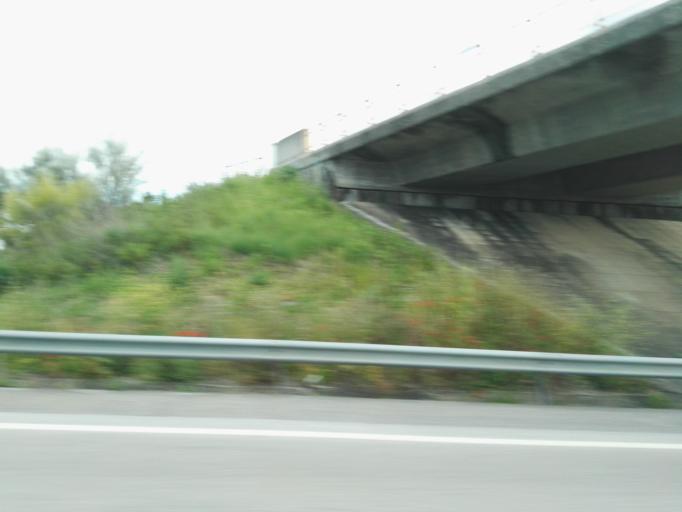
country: PT
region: Santarem
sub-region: Torres Novas
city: Torres Novas
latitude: 39.4757
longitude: -8.6046
